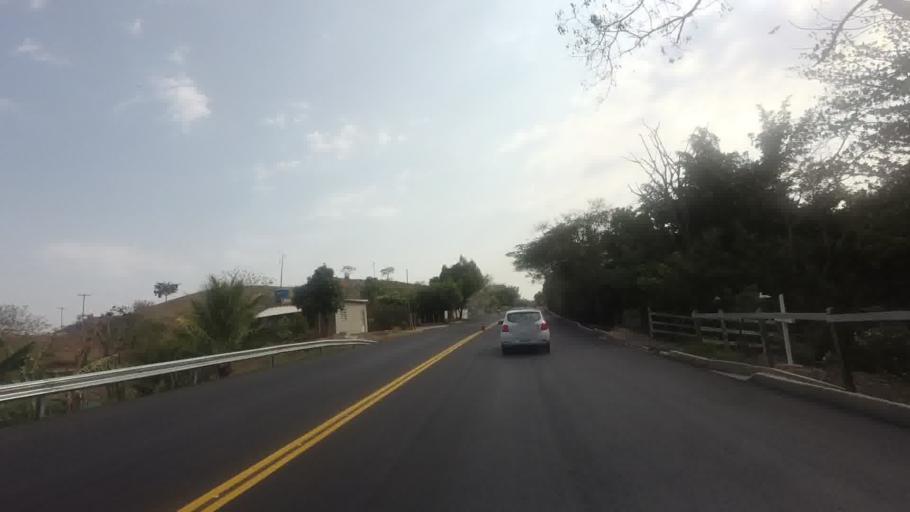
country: BR
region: Rio de Janeiro
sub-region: Bom Jesus Do Itabapoana
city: Bom Jesus do Itabapoana
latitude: -21.2017
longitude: -41.7171
